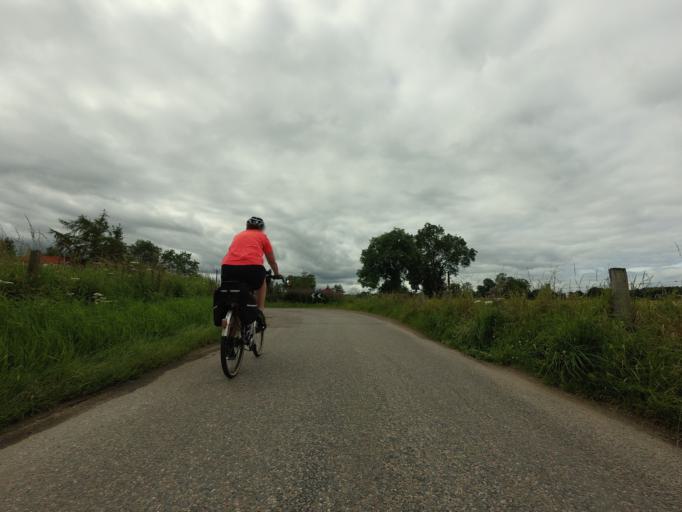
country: GB
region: Scotland
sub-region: Moray
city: Forres
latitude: 57.6167
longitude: -3.6202
